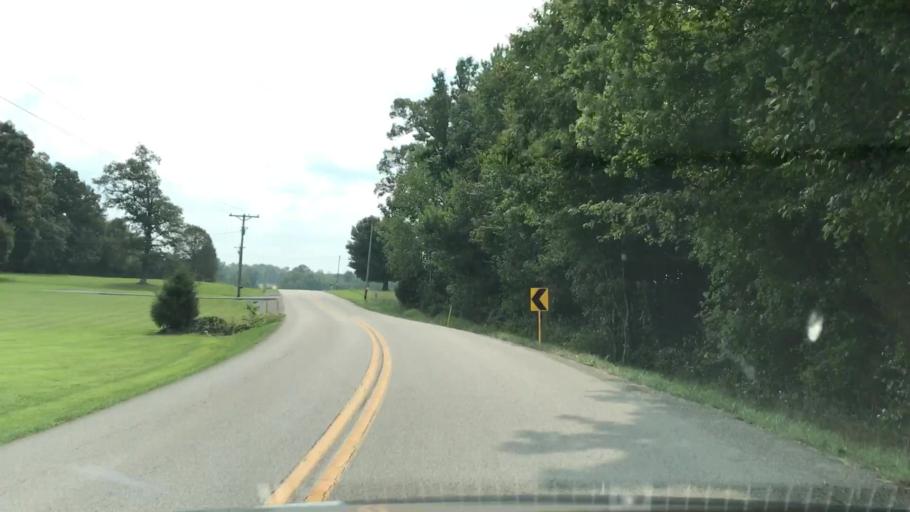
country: US
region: Kentucky
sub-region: Edmonson County
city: Brownsville
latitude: 37.1442
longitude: -86.1921
